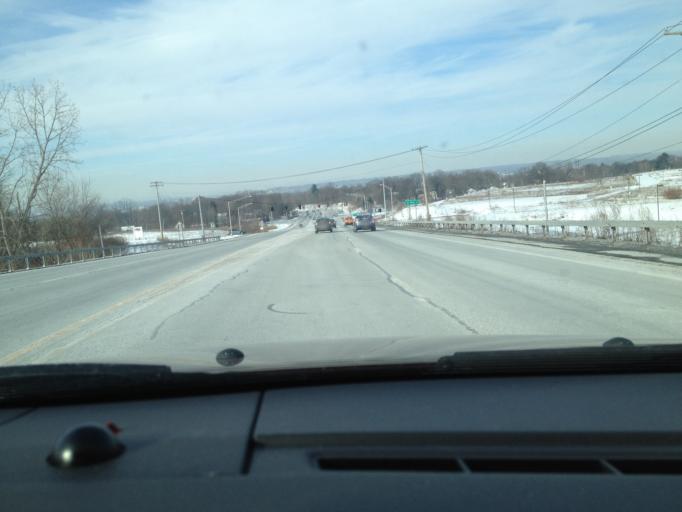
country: US
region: New York
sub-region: Rensselaer County
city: Hampton Manor
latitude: 42.6527
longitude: -73.6892
